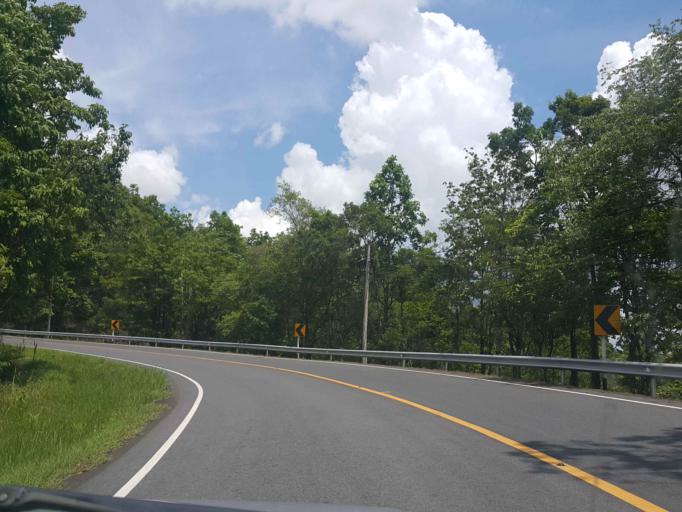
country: TH
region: Phayao
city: Chiang Muan
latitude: 18.8468
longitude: 100.3416
